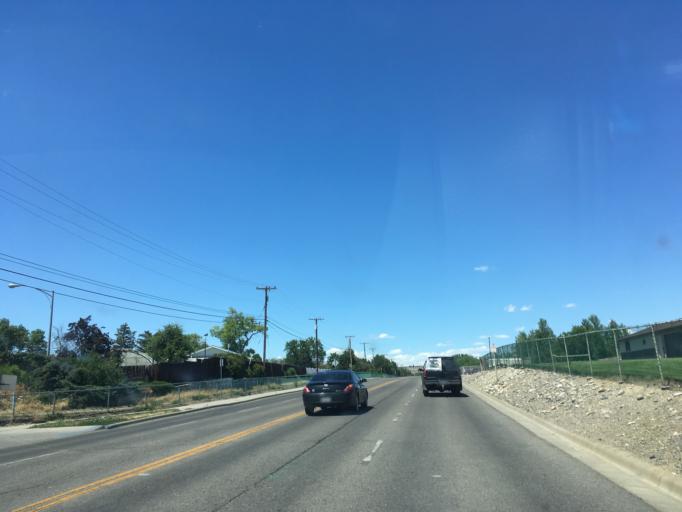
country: US
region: Montana
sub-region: Yellowstone County
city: Billings
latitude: 45.7640
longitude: -108.5650
